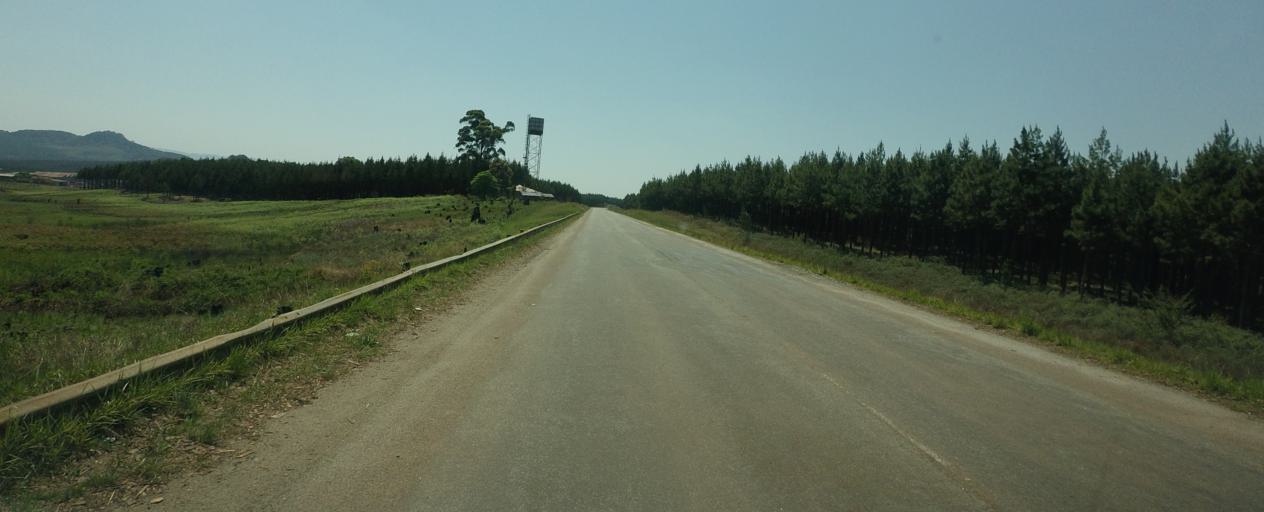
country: ZA
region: Mpumalanga
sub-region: Ehlanzeni District
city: Graksop
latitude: -24.9046
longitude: 30.8450
